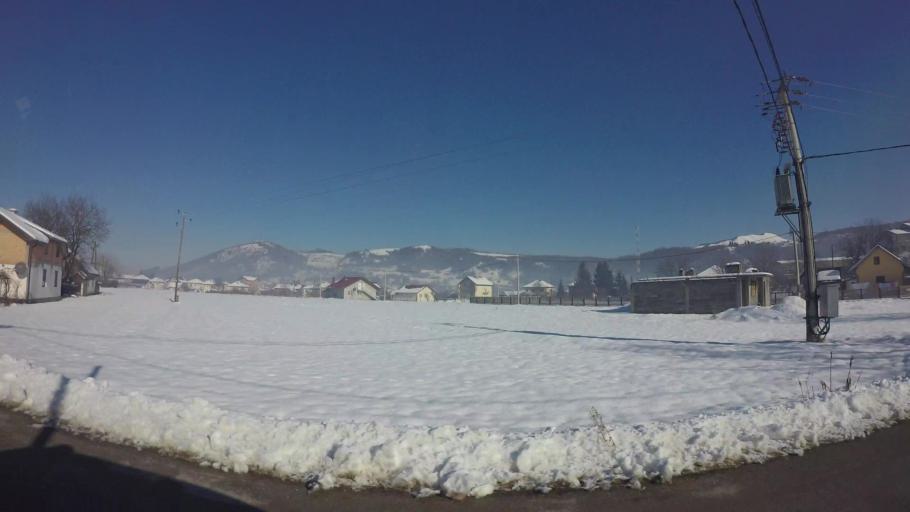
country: BA
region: Federation of Bosnia and Herzegovina
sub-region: Kanton Sarajevo
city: Sarajevo
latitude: 43.7937
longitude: 18.3512
